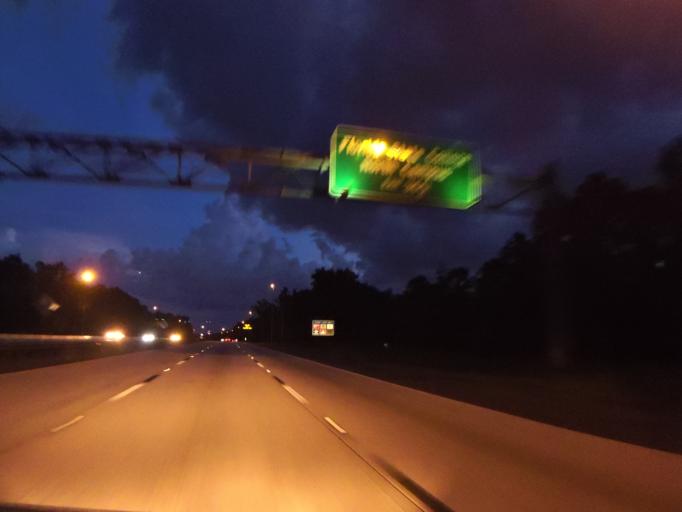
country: US
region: Florida
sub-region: Duval County
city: Jacksonville
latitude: 30.4443
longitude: -81.6540
